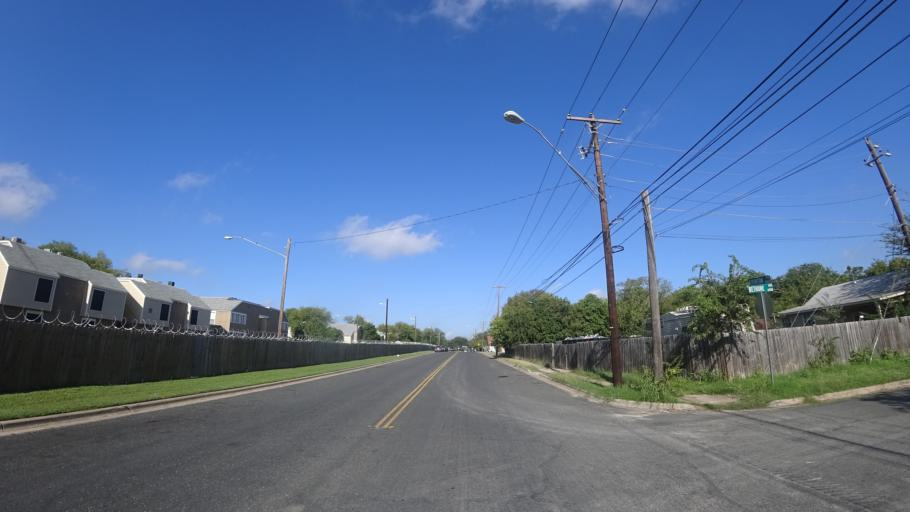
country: US
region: Texas
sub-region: Travis County
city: Austin
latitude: 30.3271
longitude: -97.7001
